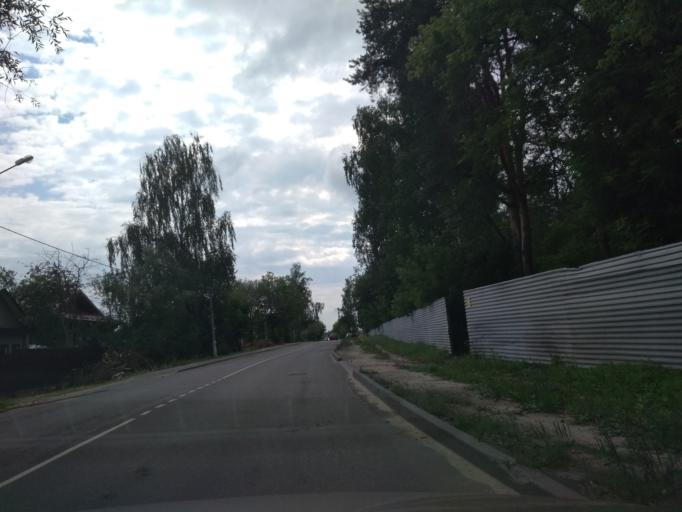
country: RU
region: Moskovskaya
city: Orekhovo-Zuyevo
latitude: 55.8042
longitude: 38.9549
